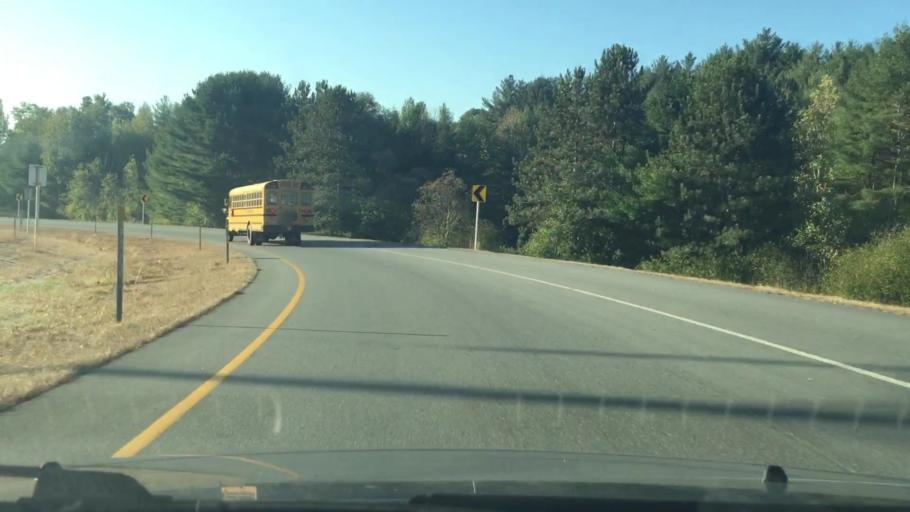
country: US
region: New Hampshire
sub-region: Cheshire County
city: Keene
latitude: 42.9429
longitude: -72.2975
